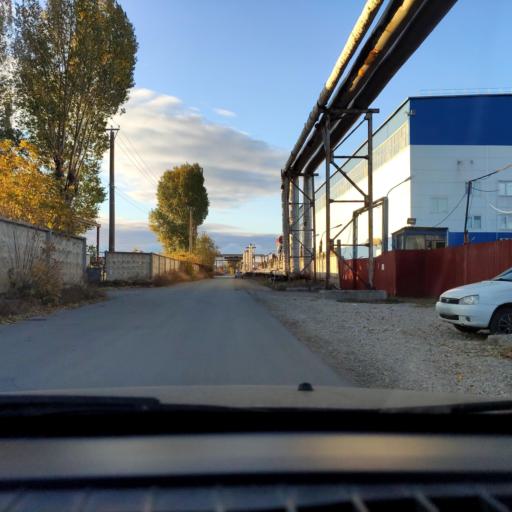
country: RU
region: Samara
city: Tol'yatti
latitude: 53.5786
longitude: 49.2634
